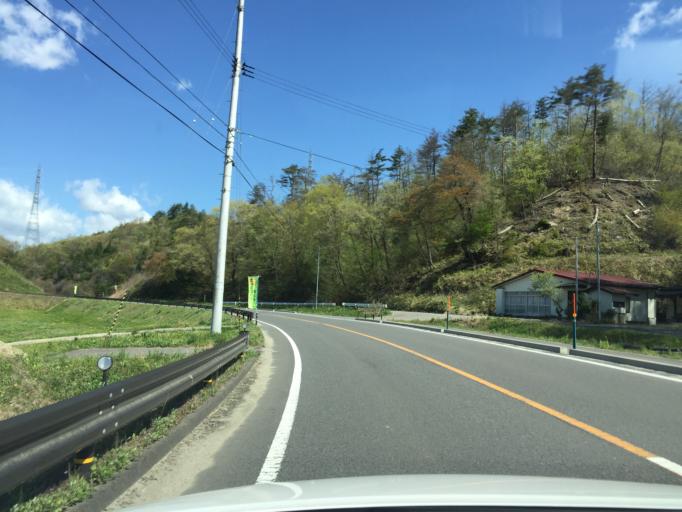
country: JP
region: Fukushima
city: Funehikimachi-funehiki
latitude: 37.5427
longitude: 140.5358
